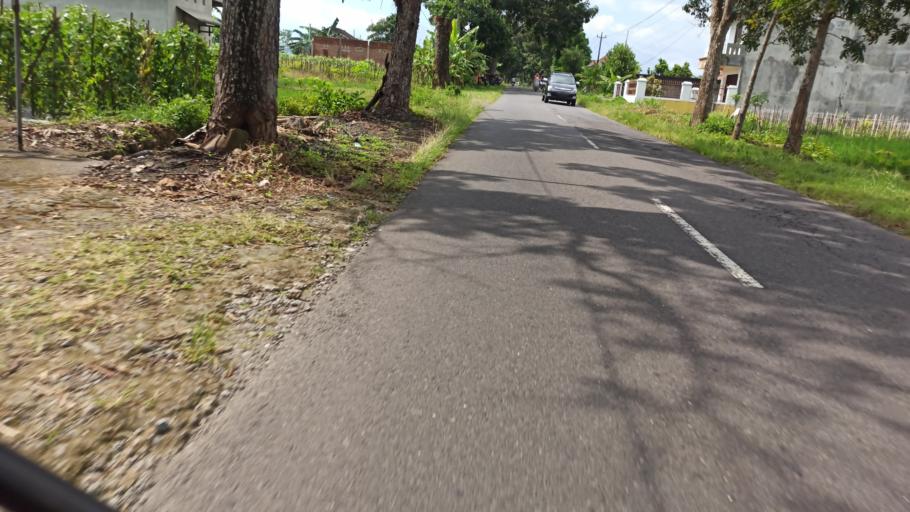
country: ID
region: Daerah Istimewa Yogyakarta
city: Sleman
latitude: -7.6927
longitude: 110.2940
